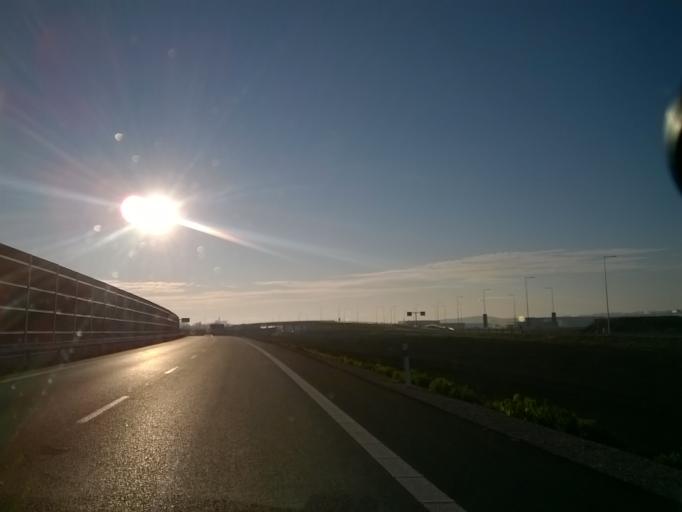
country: SK
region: Nitriansky
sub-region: Okres Nitra
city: Nitra
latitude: 48.3447
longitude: 18.0564
